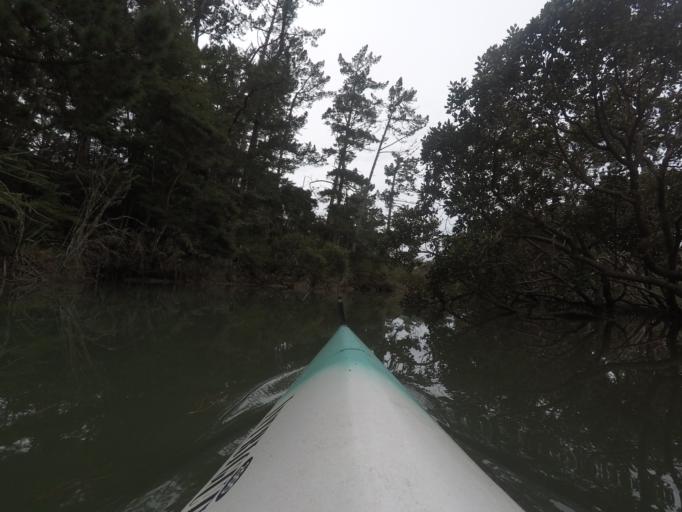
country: NZ
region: Auckland
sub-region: Auckland
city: Rothesay Bay
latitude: -36.6796
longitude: 174.7061
